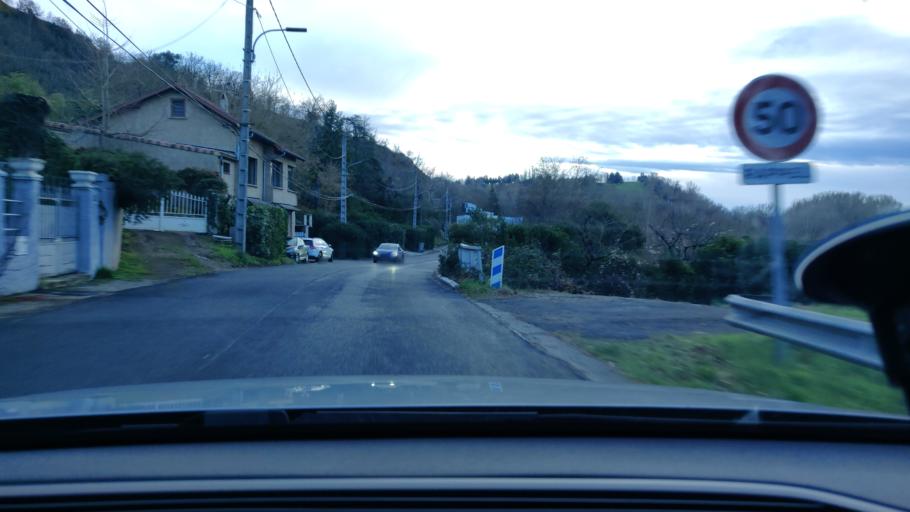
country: FR
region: Midi-Pyrenees
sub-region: Departement de la Haute-Garonne
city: Vieille-Toulouse
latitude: 43.5470
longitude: 1.4393
